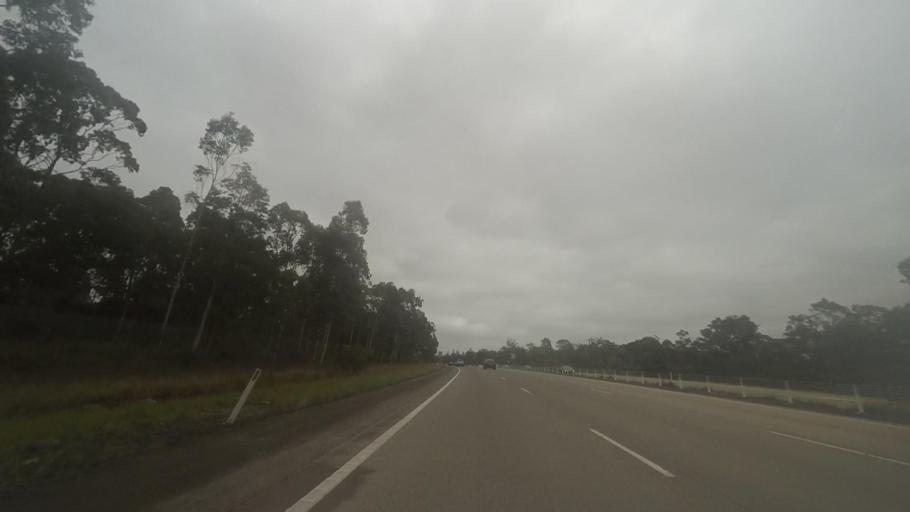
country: AU
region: New South Wales
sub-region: Port Stephens Shire
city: Medowie
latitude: -32.6830
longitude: 151.8137
